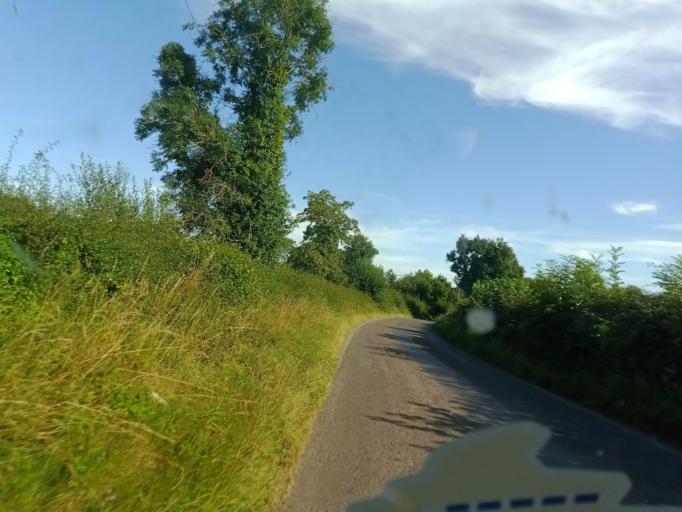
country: IE
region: Leinster
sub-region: Kilkenny
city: Ballyragget
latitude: 52.7659
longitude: -7.3912
